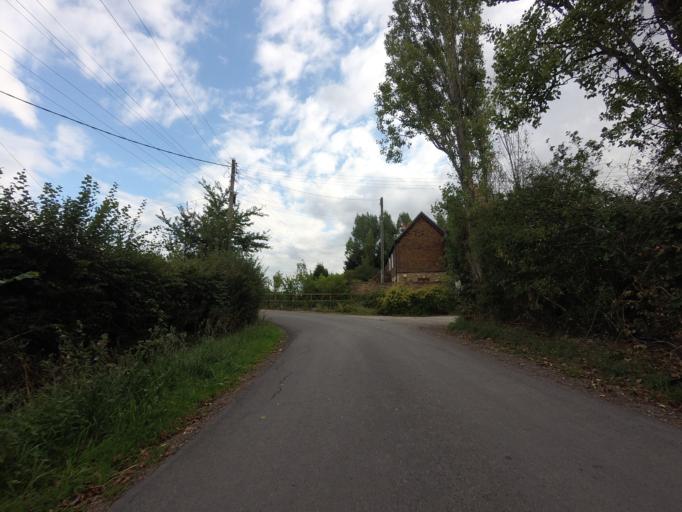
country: GB
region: England
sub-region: Kent
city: Staplehurst
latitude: 51.2081
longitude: 0.5341
